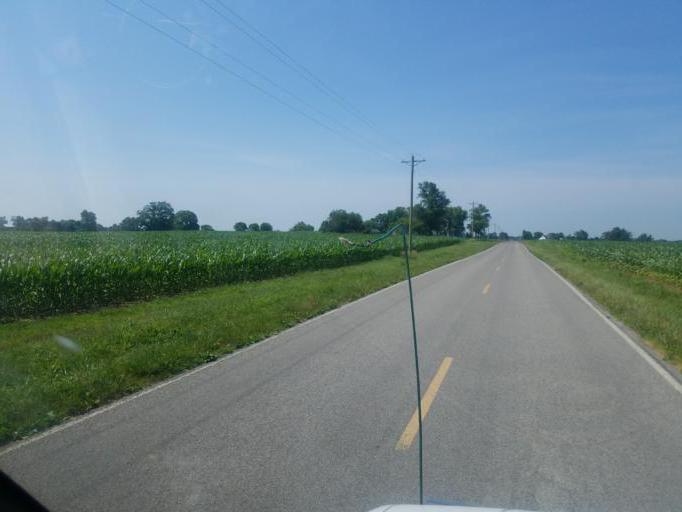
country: US
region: Ohio
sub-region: Champaign County
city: North Lewisburg
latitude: 40.1943
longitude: -83.5136
